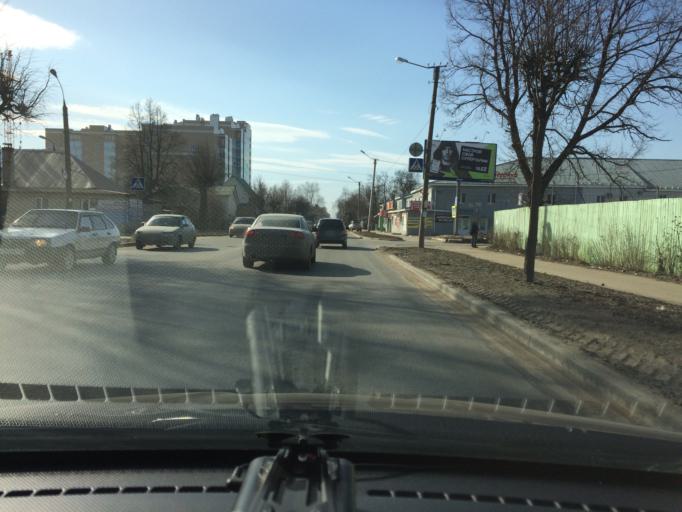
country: RU
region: Mariy-El
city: Yoshkar-Ola
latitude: 56.6494
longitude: 47.8988
